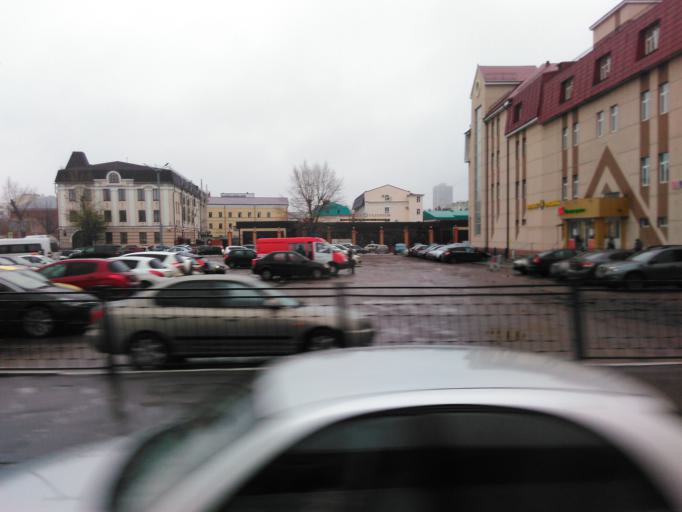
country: RU
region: Tatarstan
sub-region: Gorod Kazan'
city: Kazan
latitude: 55.7868
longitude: 49.1059
